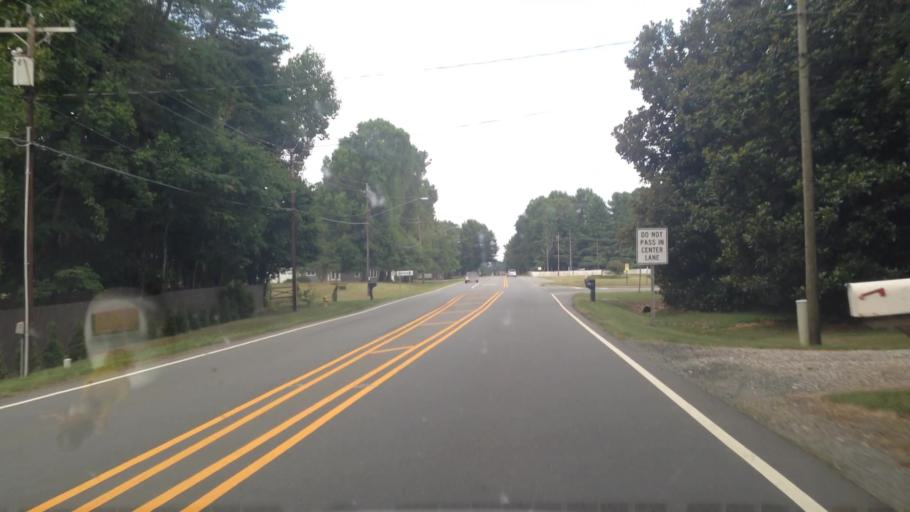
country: US
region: North Carolina
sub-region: Forsyth County
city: Walkertown
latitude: 36.1389
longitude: -80.1226
